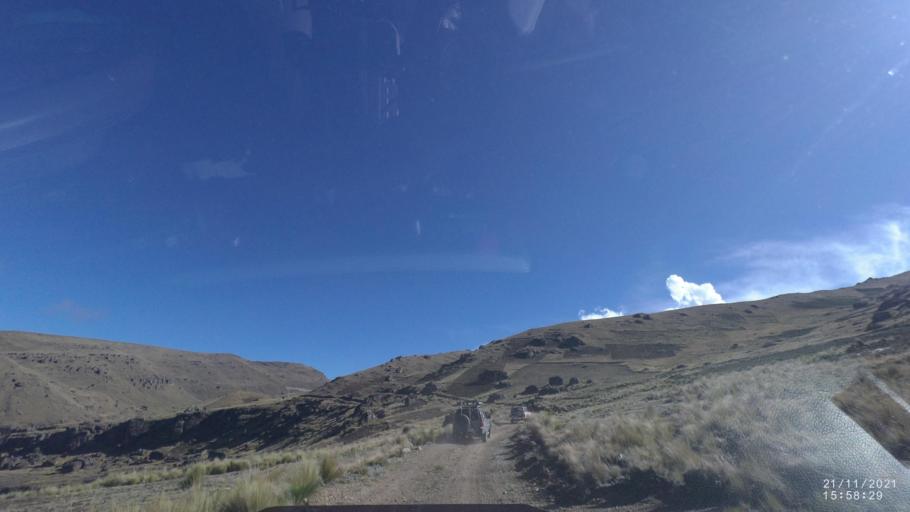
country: BO
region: Cochabamba
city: Cochabamba
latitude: -16.9779
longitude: -66.2634
